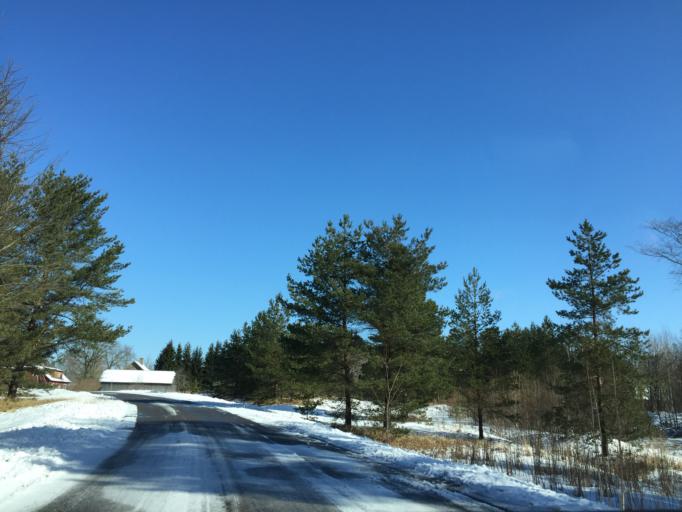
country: LV
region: Aloja
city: Staicele
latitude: 58.0245
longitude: 24.6032
